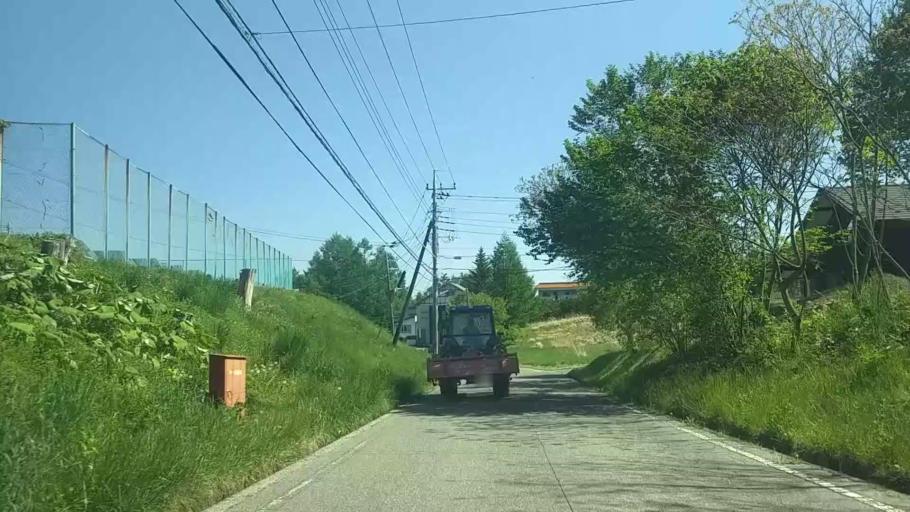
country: JP
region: Yamanashi
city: Nirasaki
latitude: 35.9047
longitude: 138.4462
